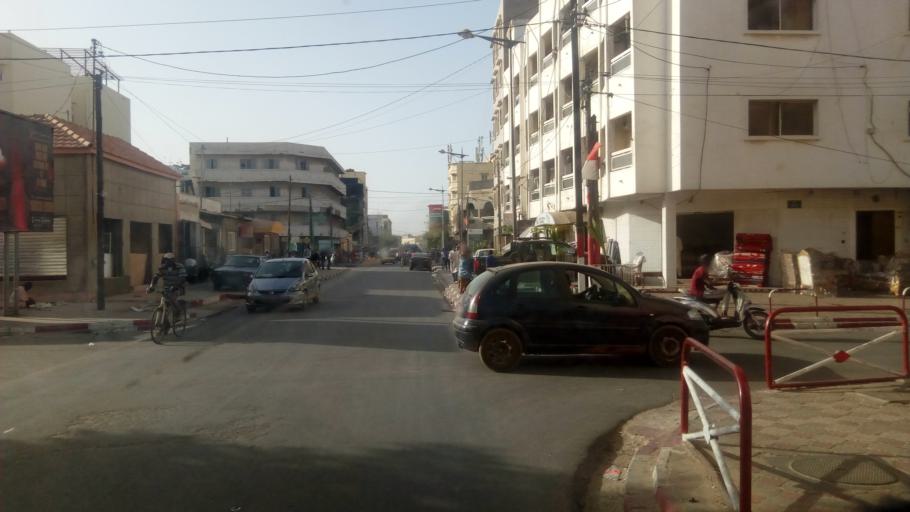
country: SN
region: Dakar
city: Dakar
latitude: 14.6845
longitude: -17.4486
